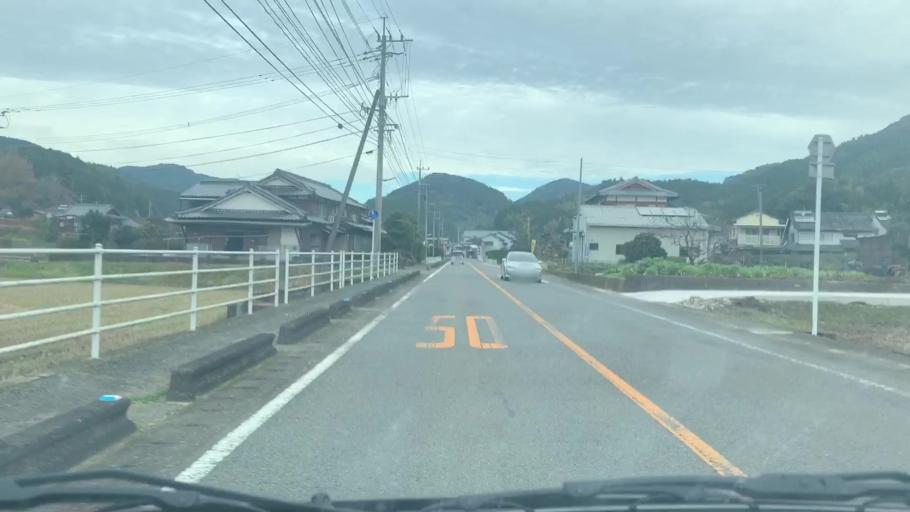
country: JP
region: Saga Prefecture
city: Ureshinomachi-shimojuku
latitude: 33.1446
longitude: 129.9764
